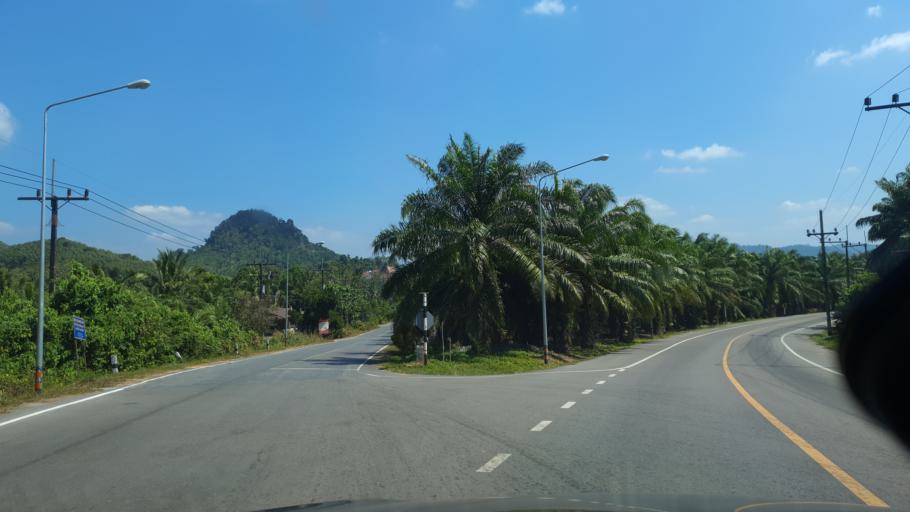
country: TH
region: Krabi
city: Khlong Thom
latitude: 7.9534
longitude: 99.2024
